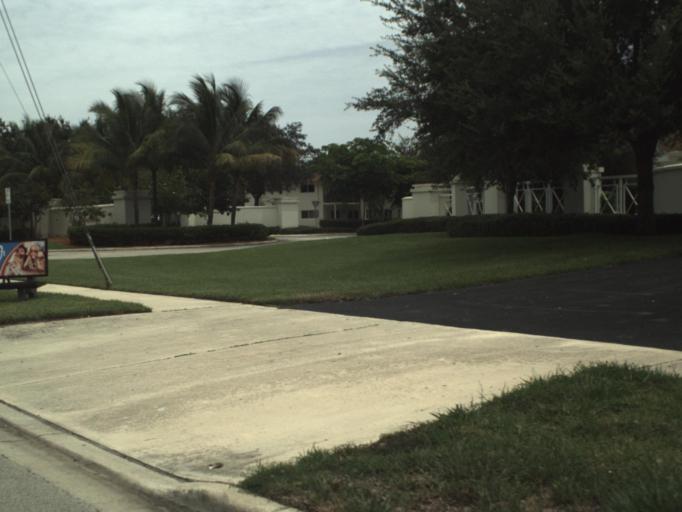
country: US
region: Florida
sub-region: Broward County
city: Lauderdale-by-the-Sea
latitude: 26.1942
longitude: -80.1125
